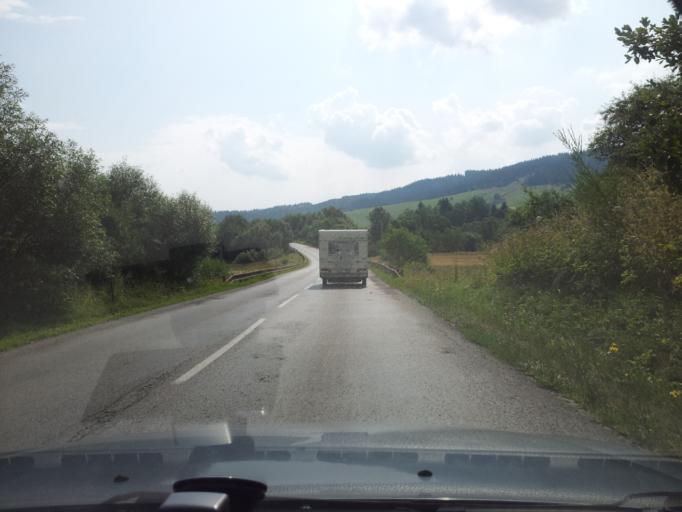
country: SK
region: Zilinsky
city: Oravska Lesna
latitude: 49.3798
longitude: 19.3304
